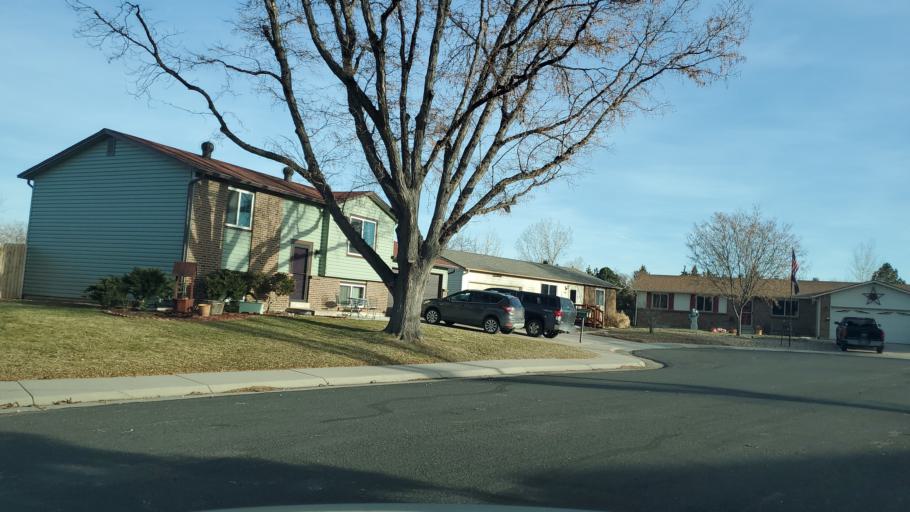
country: US
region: Colorado
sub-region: Adams County
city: Northglenn
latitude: 39.9082
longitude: -104.9441
